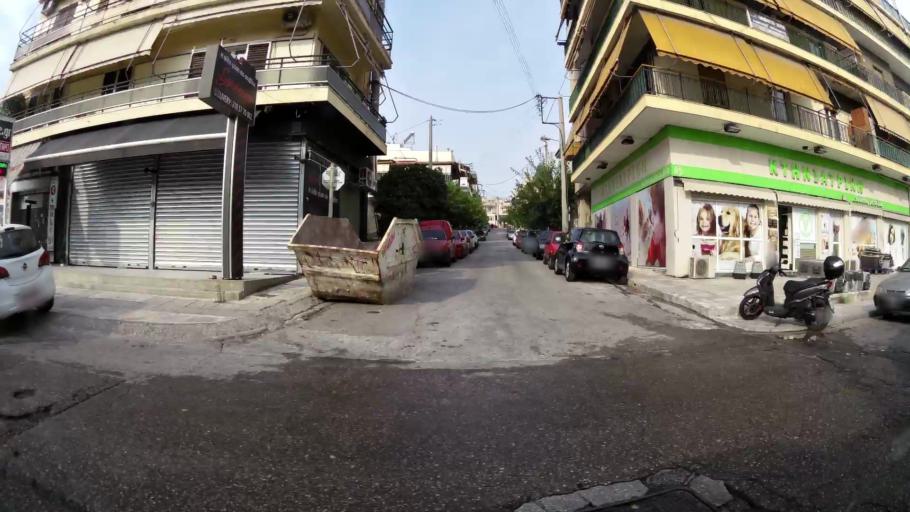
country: GR
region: Attica
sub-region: Nomarchia Athinas
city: Peristeri
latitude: 38.0070
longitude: 23.6879
